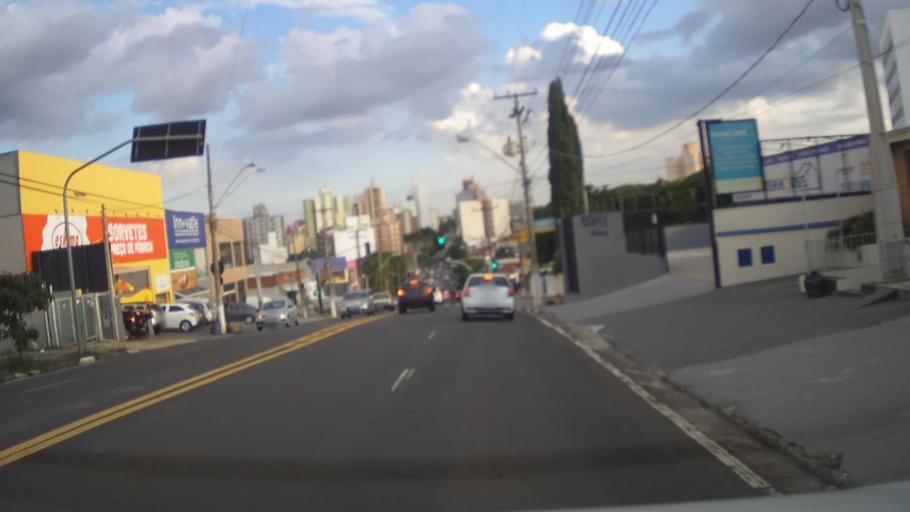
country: BR
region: Sao Paulo
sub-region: Campinas
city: Campinas
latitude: -22.8969
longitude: -47.0732
